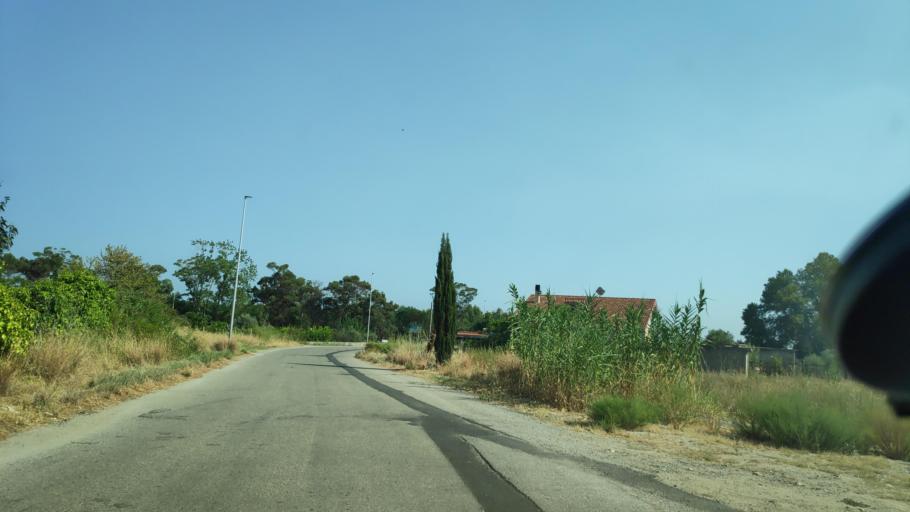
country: IT
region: Calabria
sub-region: Provincia di Catanzaro
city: Badolato Marina
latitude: 38.5798
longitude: 16.5672
